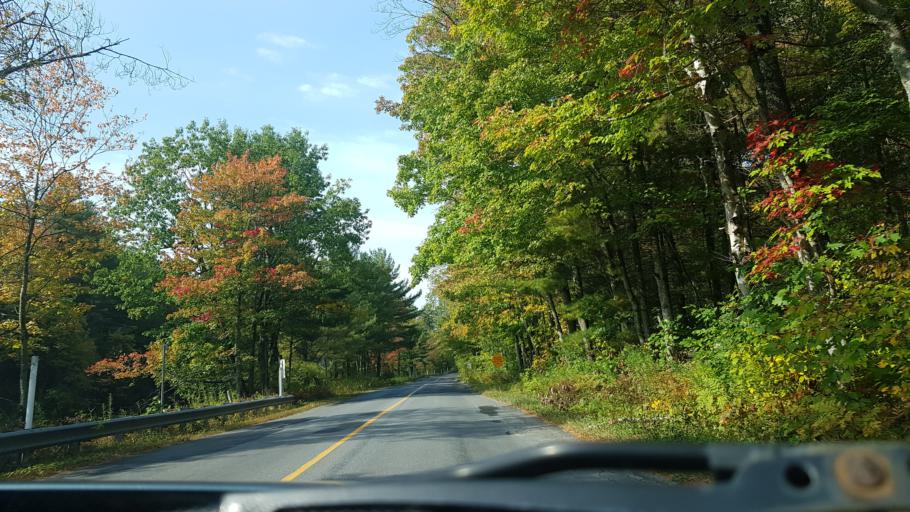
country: CA
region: Ontario
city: Gravenhurst
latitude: 44.7913
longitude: -79.2175
